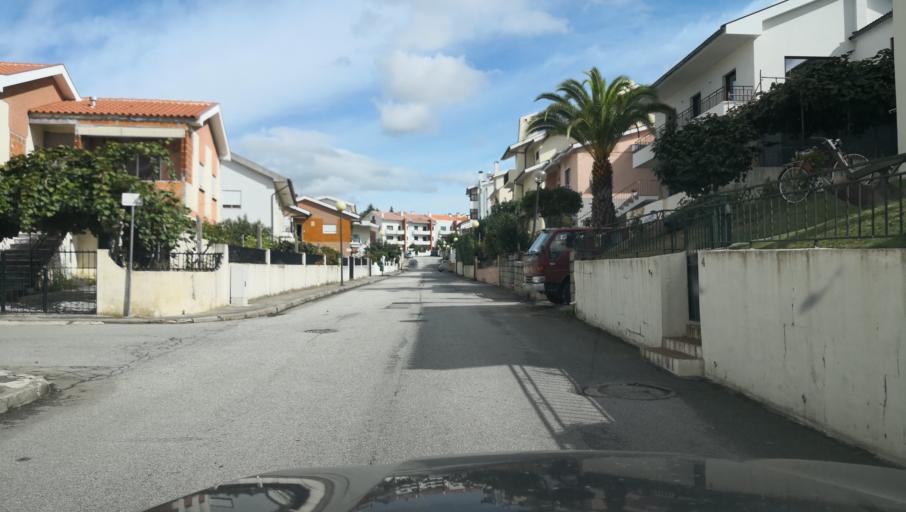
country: PT
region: Vila Real
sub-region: Vila Real
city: Vila Real
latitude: 41.2920
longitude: -7.7284
